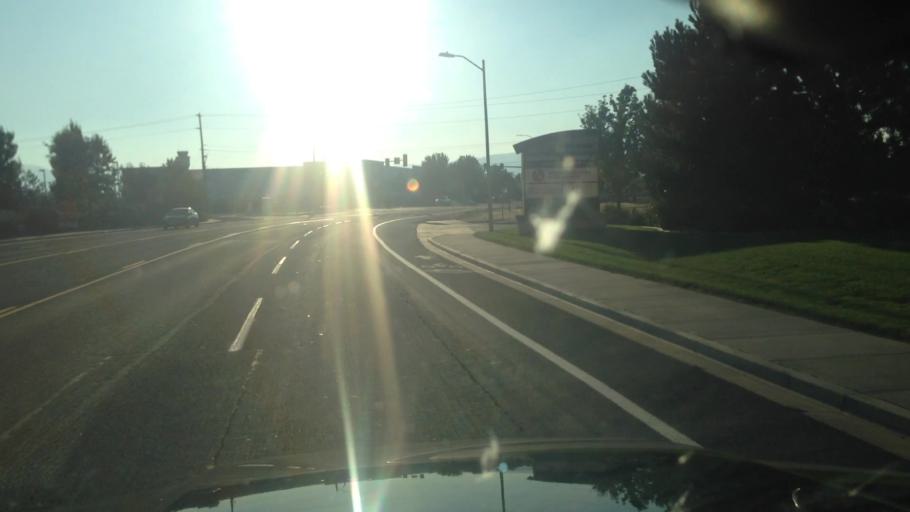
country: US
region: Nevada
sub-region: Washoe County
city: Sparks
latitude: 39.4982
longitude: -119.7504
